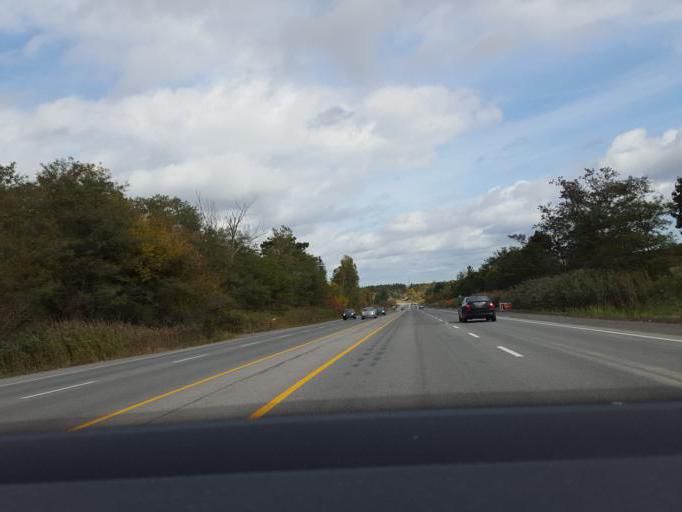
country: CA
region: Ontario
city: Pickering
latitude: 43.8787
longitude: -79.1131
